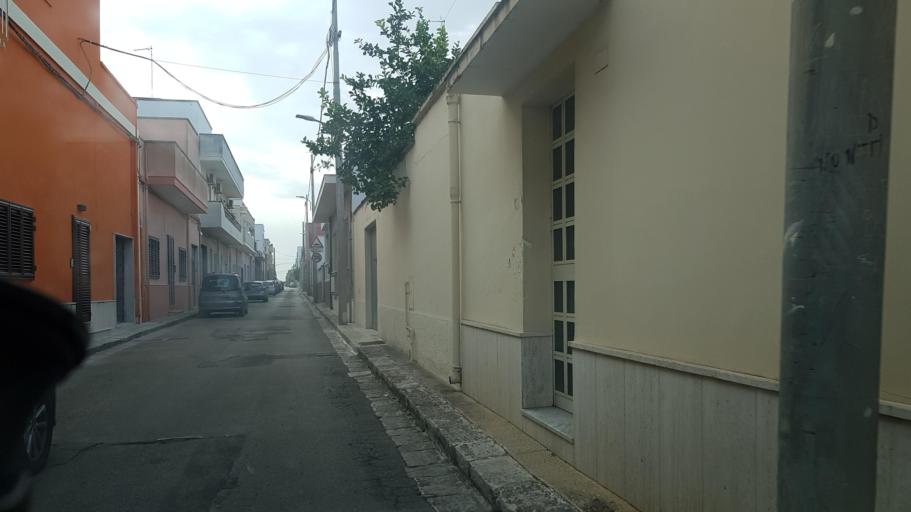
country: IT
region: Apulia
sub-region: Provincia di Lecce
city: Trepuzzi
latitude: 40.4091
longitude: 18.0701
